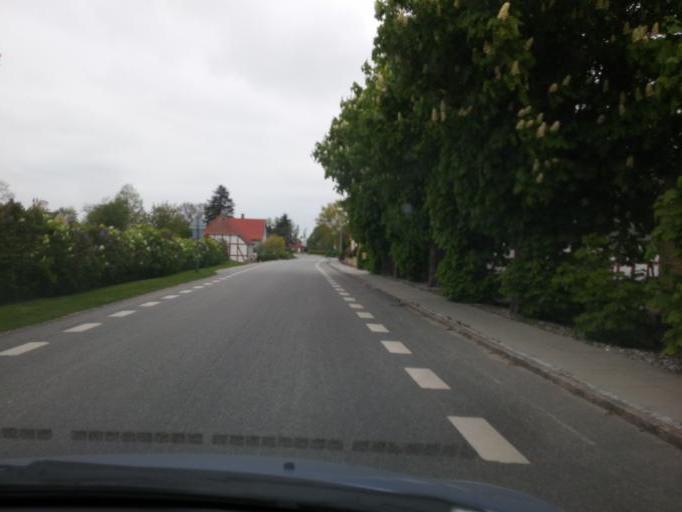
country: DK
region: South Denmark
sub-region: Kerteminde Kommune
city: Langeskov
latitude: 55.4058
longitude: 10.5842
